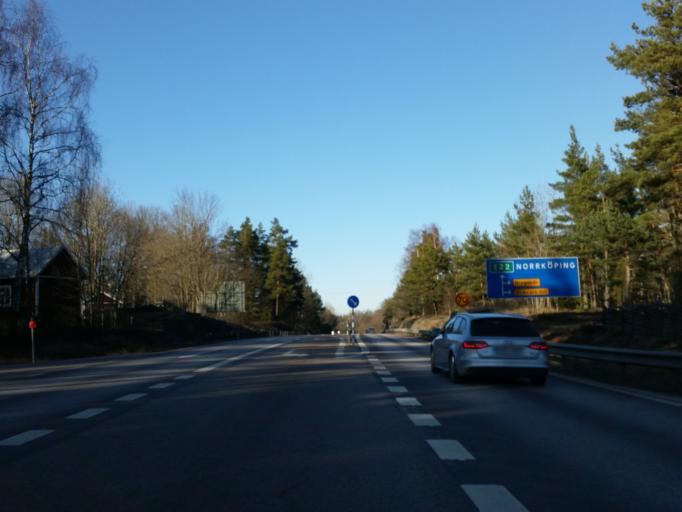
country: SE
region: Kalmar
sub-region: Oskarshamns Kommun
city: Oskarshamn
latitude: 57.3343
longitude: 16.4803
